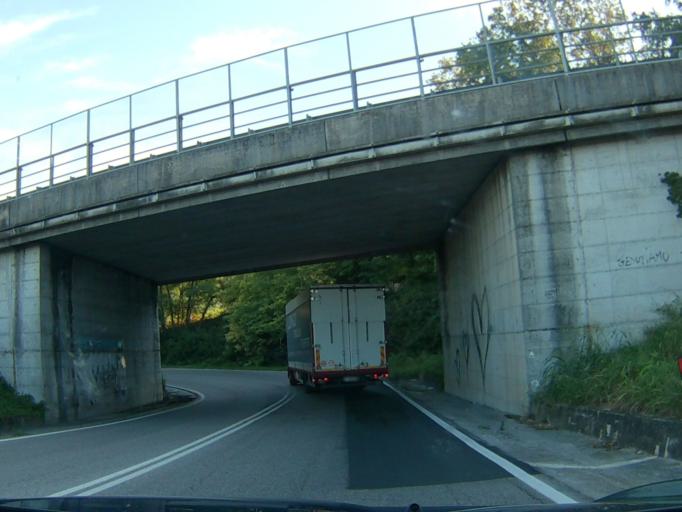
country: IT
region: Lombardy
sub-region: Provincia di Brescia
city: Lonato
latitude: 45.4605
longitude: 10.5110
